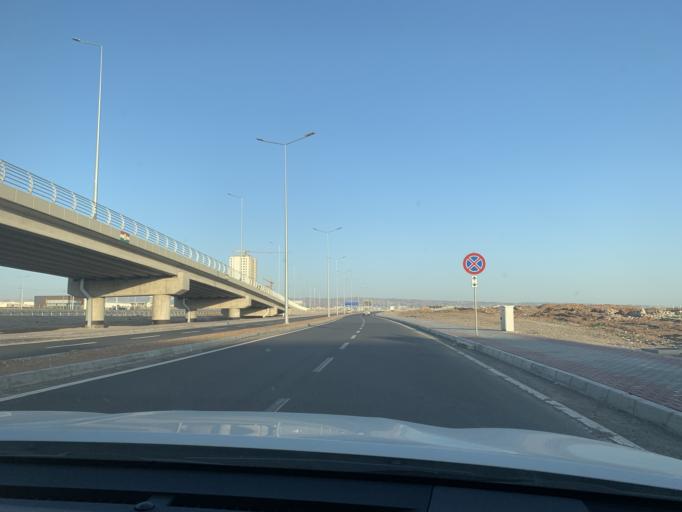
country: IQ
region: Arbil
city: Erbil
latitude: 36.2876
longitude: 44.0345
